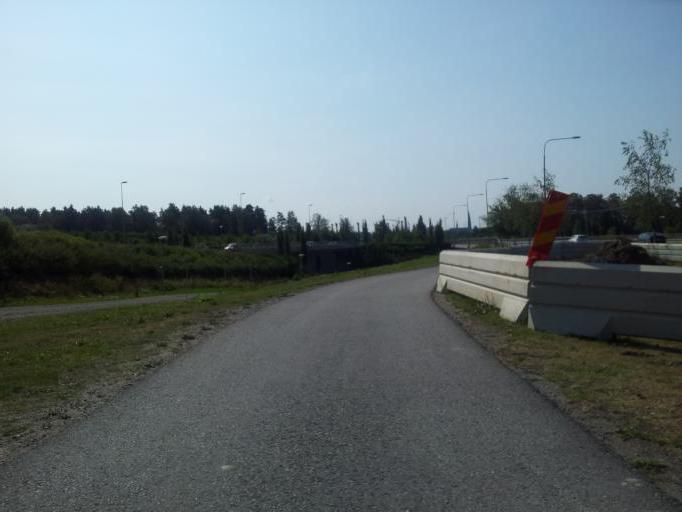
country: SE
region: Uppsala
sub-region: Uppsala Kommun
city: Gamla Uppsala
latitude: 59.8818
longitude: 17.6358
